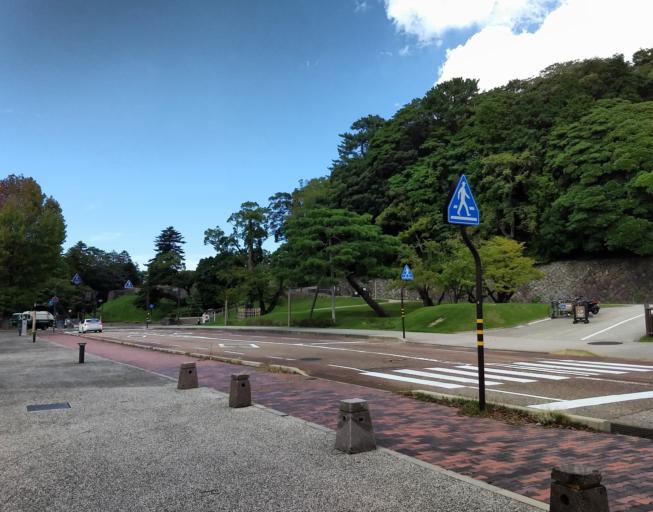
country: JP
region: Ishikawa
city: Kanazawa-shi
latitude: 36.5636
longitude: 136.6575
